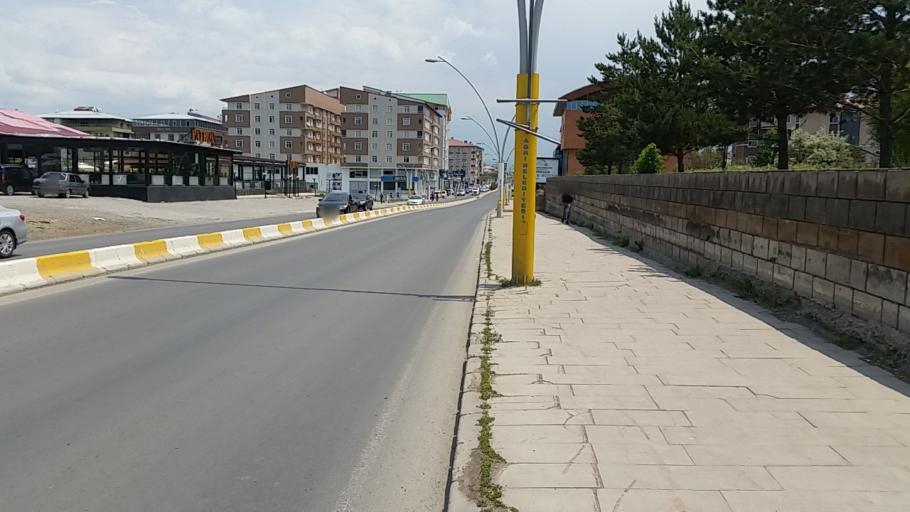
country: TR
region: Agri
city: Agri
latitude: 39.7188
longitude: 43.0282
